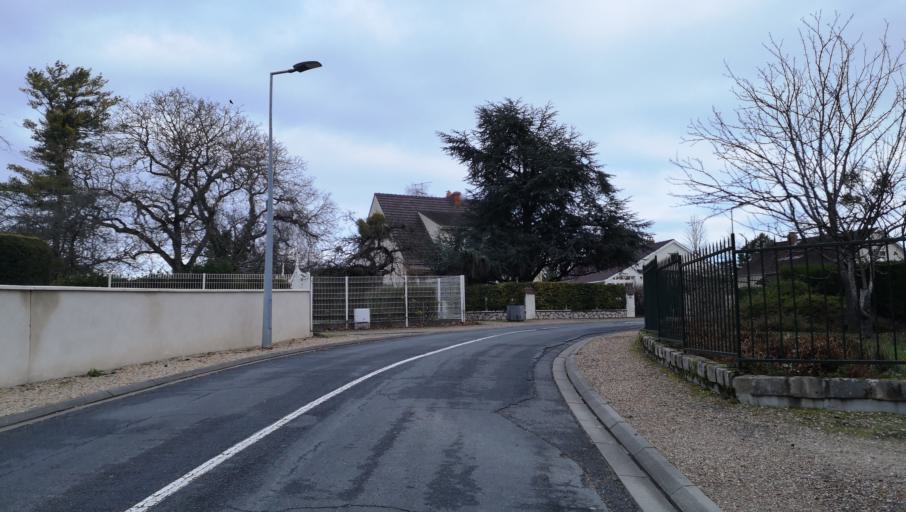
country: FR
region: Centre
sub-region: Departement du Loiret
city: Saint-Jean-de-Braye
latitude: 47.9016
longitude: 1.9891
